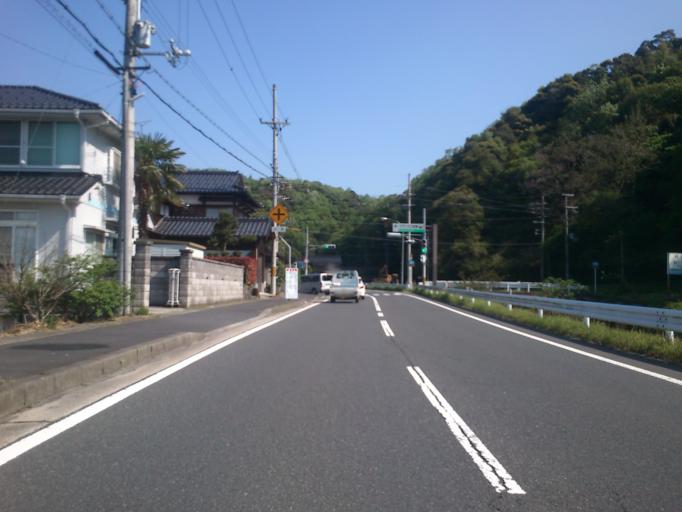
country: JP
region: Kyoto
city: Miyazu
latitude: 35.5748
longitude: 135.1605
